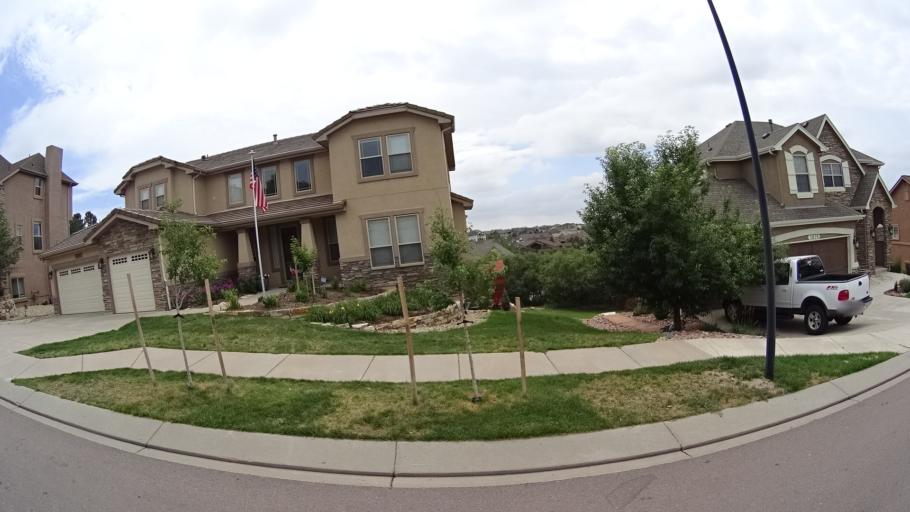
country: US
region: Colorado
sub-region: El Paso County
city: Gleneagle
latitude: 39.0150
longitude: -104.7969
